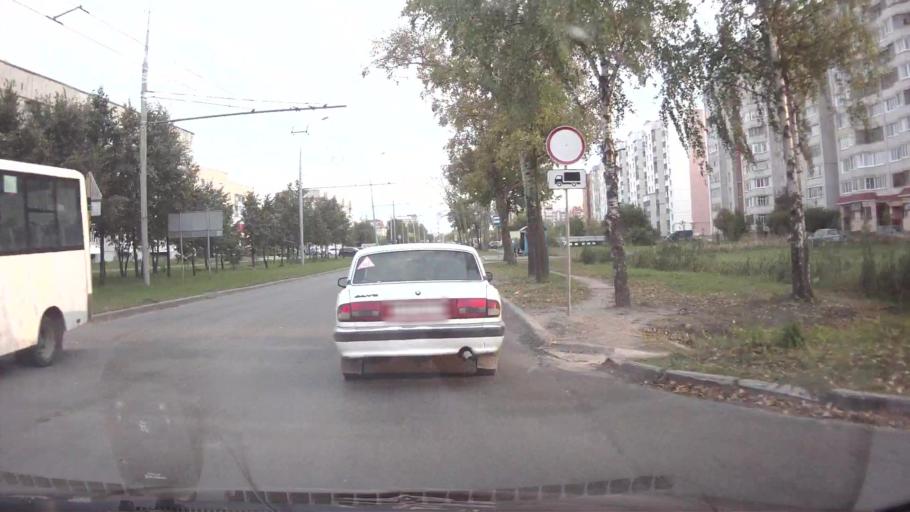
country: RU
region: Mariy-El
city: Yoshkar-Ola
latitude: 56.6516
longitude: 47.8549
